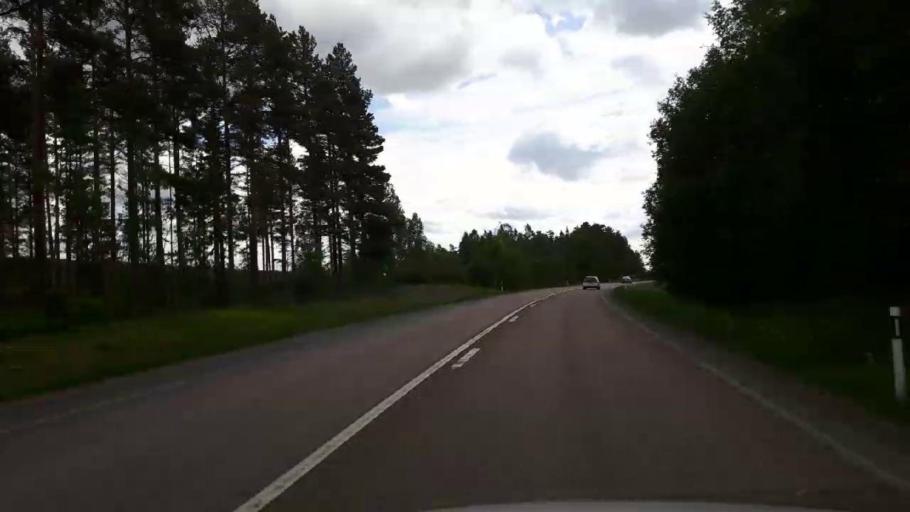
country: SE
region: Dalarna
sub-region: Saters Kommun
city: Saeter
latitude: 60.4693
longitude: 15.7972
